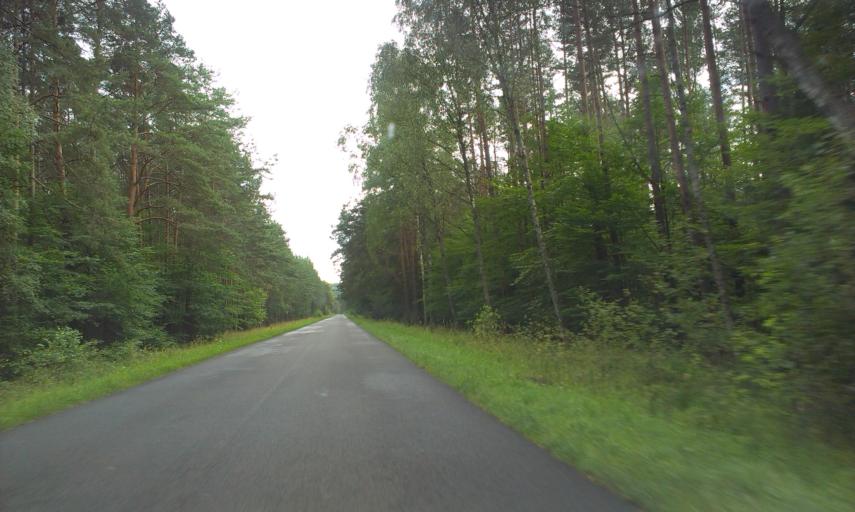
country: PL
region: Greater Poland Voivodeship
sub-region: Powiat zlotowski
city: Okonek
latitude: 53.5007
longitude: 16.9804
